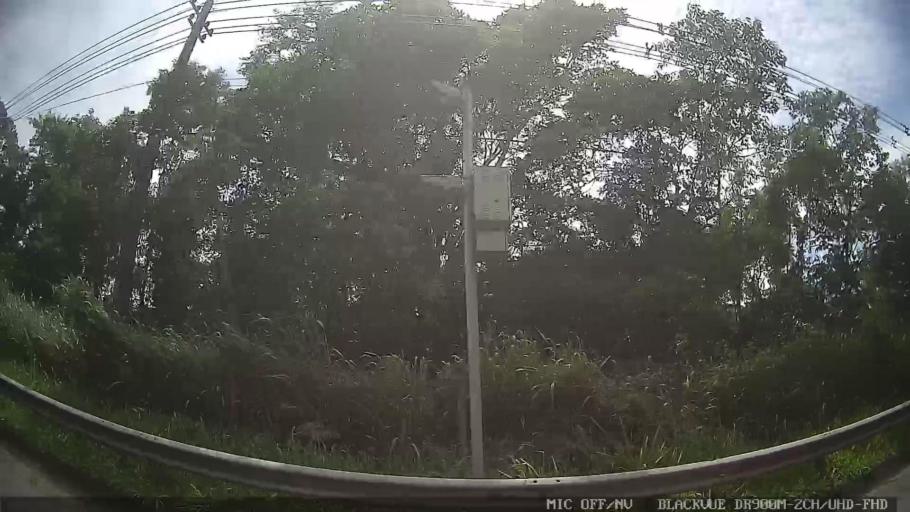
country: BR
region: Sao Paulo
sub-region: Mogi das Cruzes
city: Mogi das Cruzes
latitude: -23.4558
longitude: -46.2460
